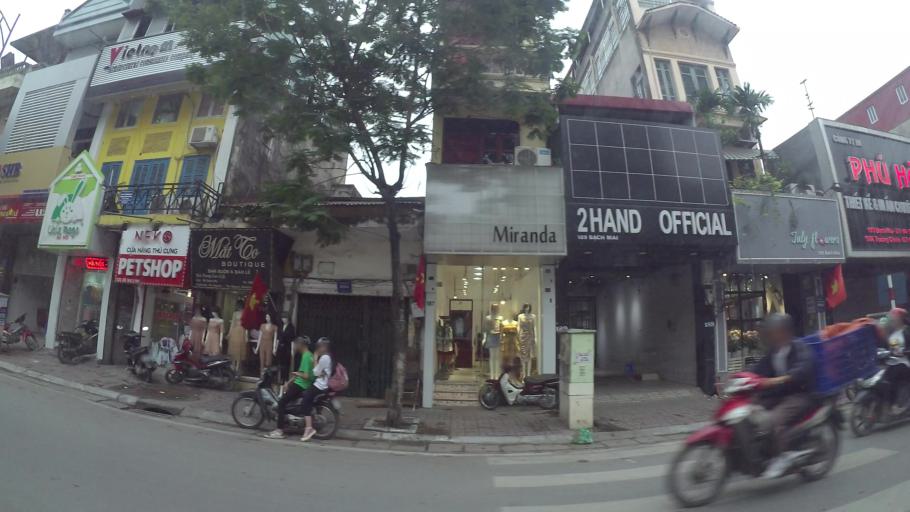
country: VN
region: Ha Noi
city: Hai BaTrung
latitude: 21.0049
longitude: 105.8512
